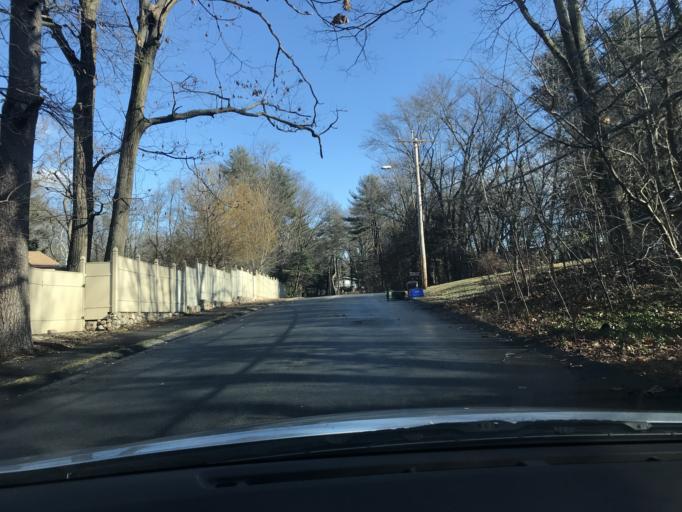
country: US
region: Massachusetts
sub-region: Middlesex County
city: Lexington
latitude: 42.4746
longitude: -71.2327
